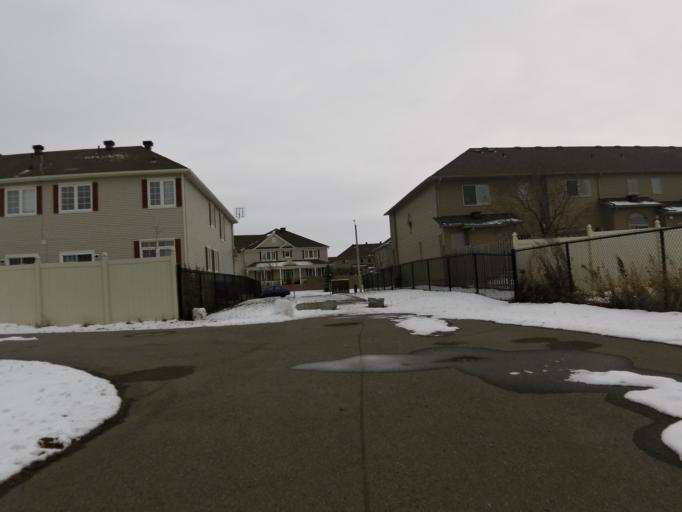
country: CA
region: Ontario
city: Bells Corners
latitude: 45.2790
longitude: -75.8688
